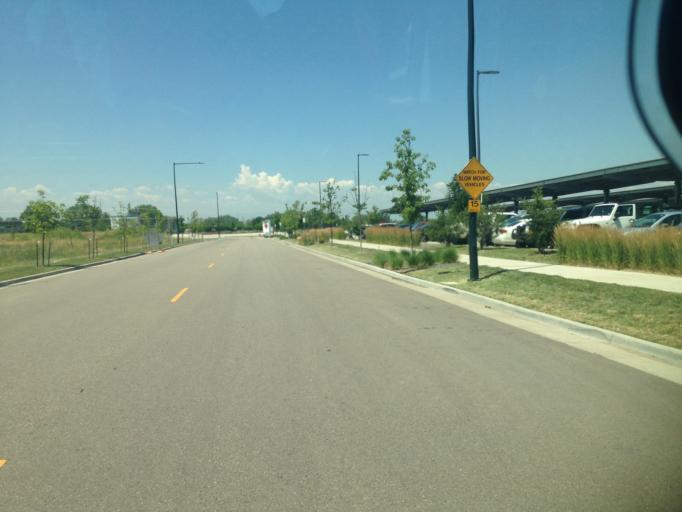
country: US
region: Colorado
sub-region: Adams County
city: Aurora
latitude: 39.8074
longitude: -104.7817
